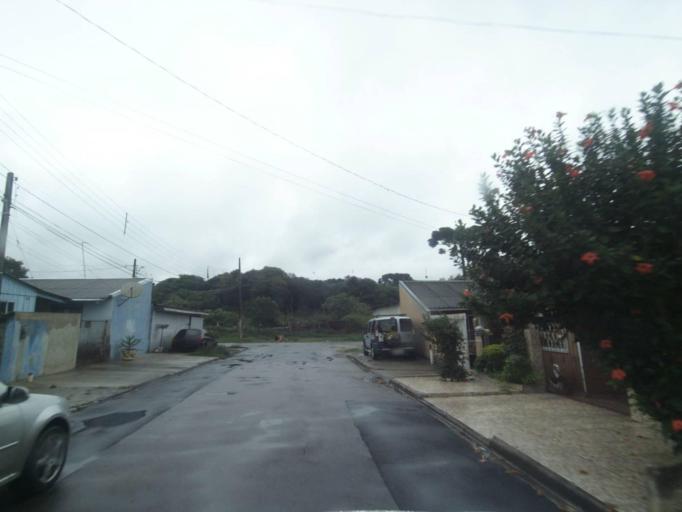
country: BR
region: Parana
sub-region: Araucaria
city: Araucaria
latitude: -25.5336
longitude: -49.3397
